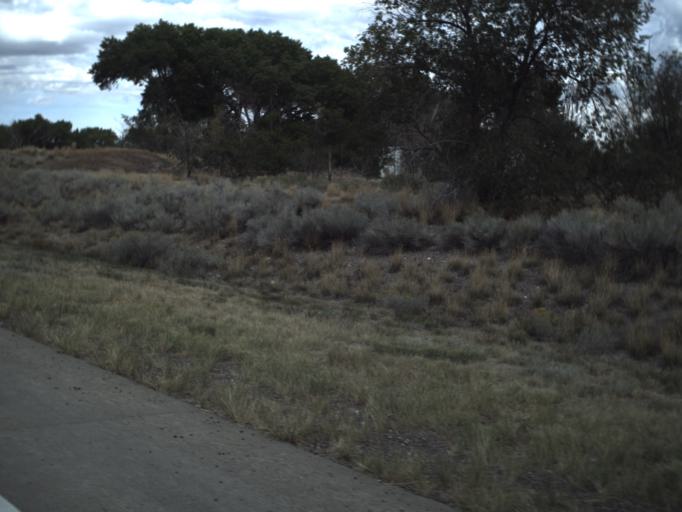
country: US
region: Utah
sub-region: Sevier County
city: Monroe
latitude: 38.6867
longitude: -112.1530
